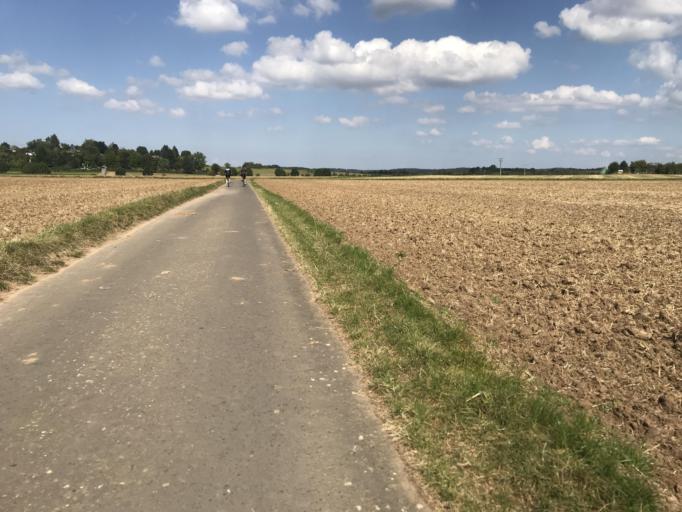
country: DE
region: Hesse
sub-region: Regierungsbezirk Giessen
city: Hungen
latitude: 50.4428
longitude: 8.9177
